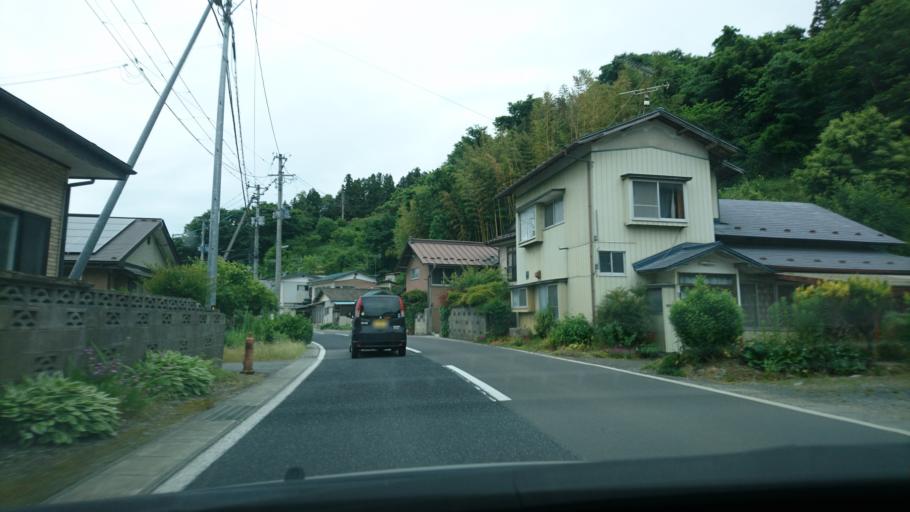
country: JP
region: Iwate
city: Ichinoseki
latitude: 38.9596
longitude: 141.2540
